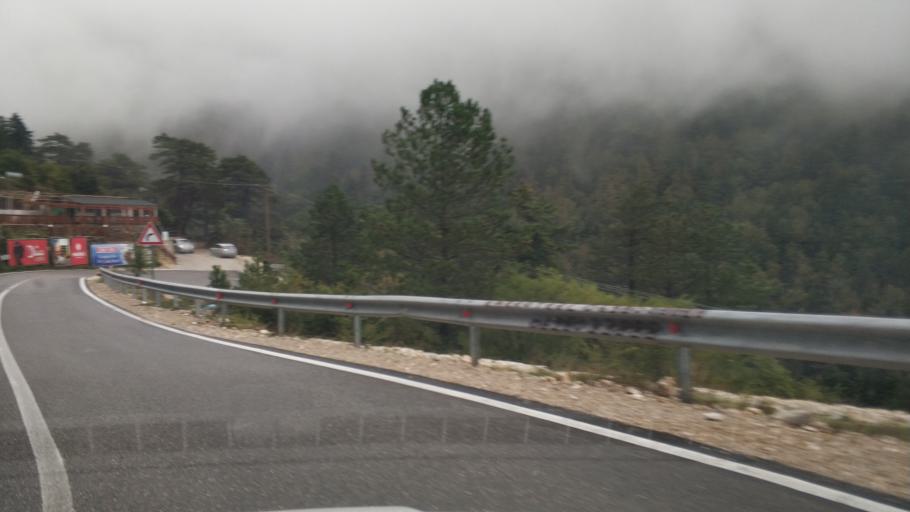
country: AL
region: Vlore
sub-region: Rrethi i Vlores
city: Vranisht
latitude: 40.2039
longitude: 19.5876
